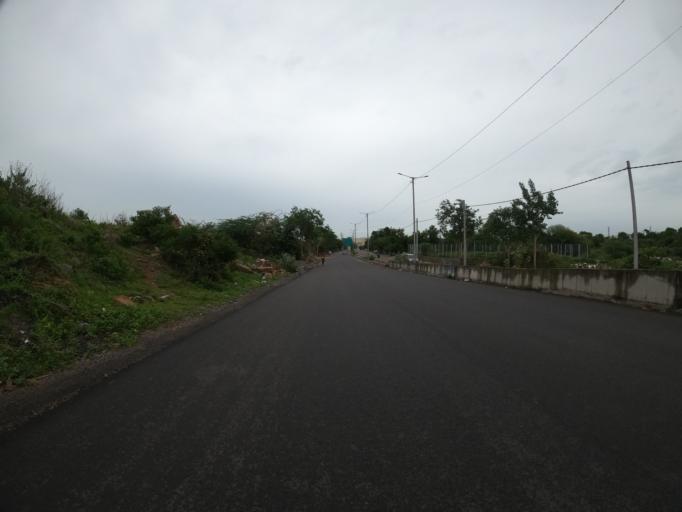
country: IN
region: Telangana
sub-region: Rangareddi
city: Kukatpalli
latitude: 17.4604
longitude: 78.3939
